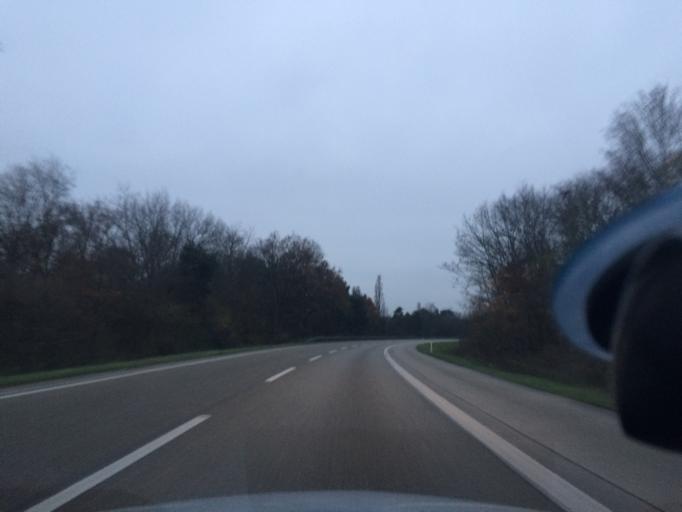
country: DE
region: Hesse
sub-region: Regierungsbezirk Darmstadt
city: Nauheim
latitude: 49.9812
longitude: 8.4646
